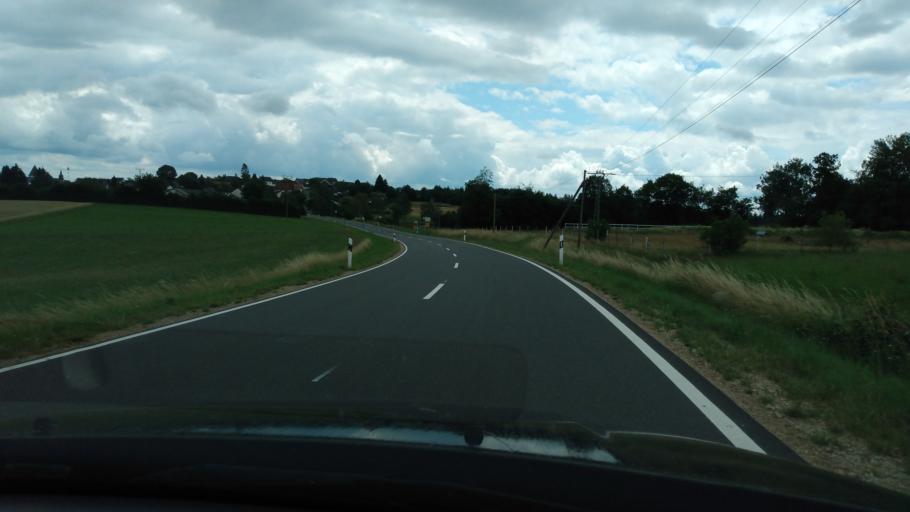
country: DE
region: Rheinland-Pfalz
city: Bleckhausen
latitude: 50.1307
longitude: 6.7712
